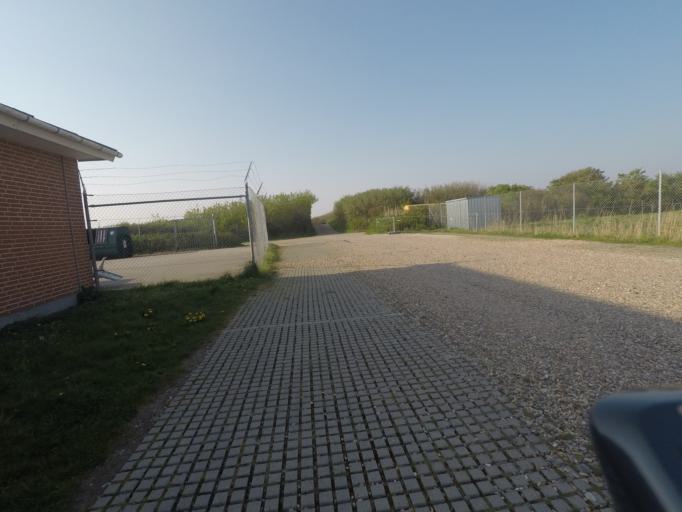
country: DE
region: Schleswig-Holstein
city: List
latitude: 55.1466
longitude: 8.4984
